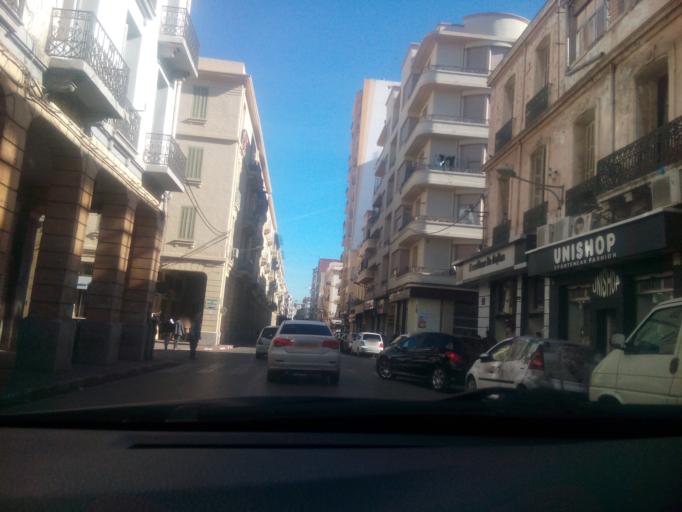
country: DZ
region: Oran
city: Oran
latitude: 35.7024
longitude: -0.6411
